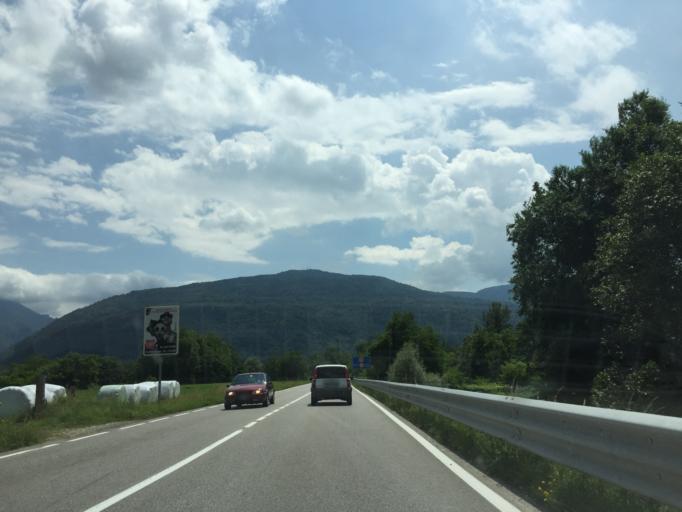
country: IT
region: Veneto
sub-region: Provincia di Belluno
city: Fonzaso
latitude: 46.0146
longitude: 11.7917
